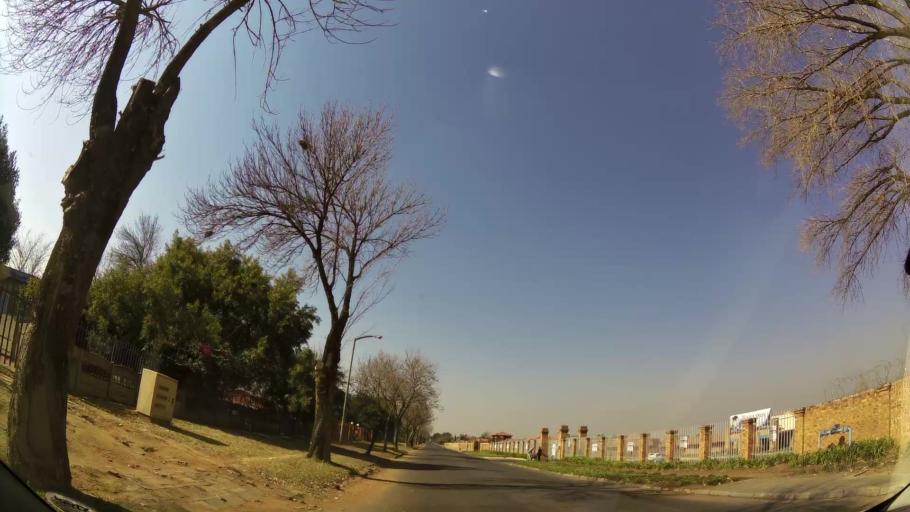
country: ZA
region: Gauteng
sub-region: Ekurhuleni Metropolitan Municipality
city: Boksburg
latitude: -26.1663
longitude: 28.2670
